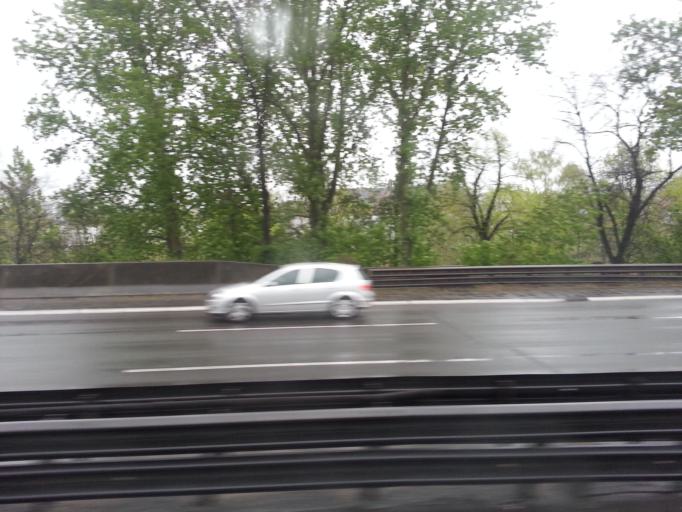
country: DE
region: Berlin
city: Charlottenburg Bezirk
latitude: 52.5229
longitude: 13.2813
